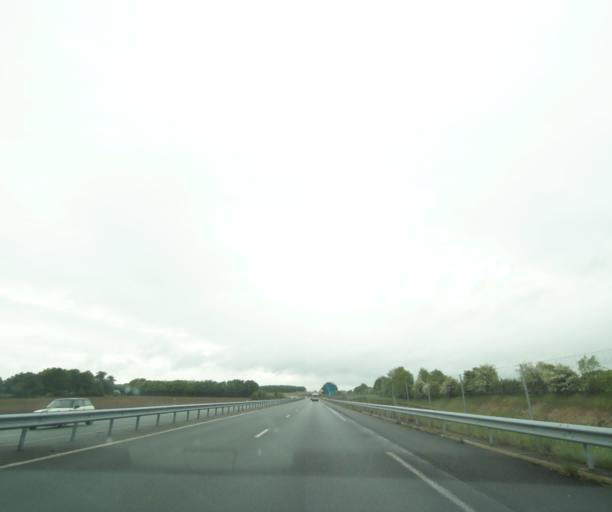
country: FR
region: Poitou-Charentes
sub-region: Departement de la Charente-Maritime
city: Chermignac
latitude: 45.7146
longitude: -0.6762
